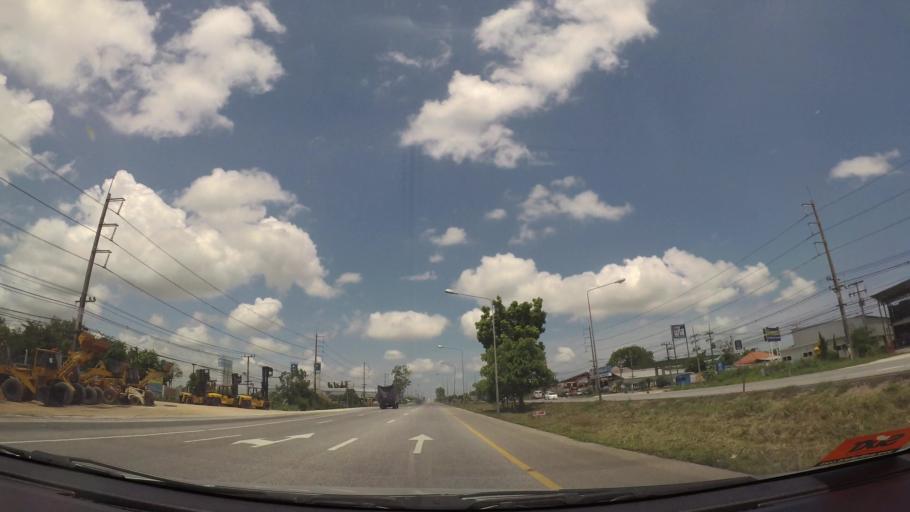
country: TH
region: Rayong
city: Nikhom Phattana
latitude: 12.7800
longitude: 101.1651
